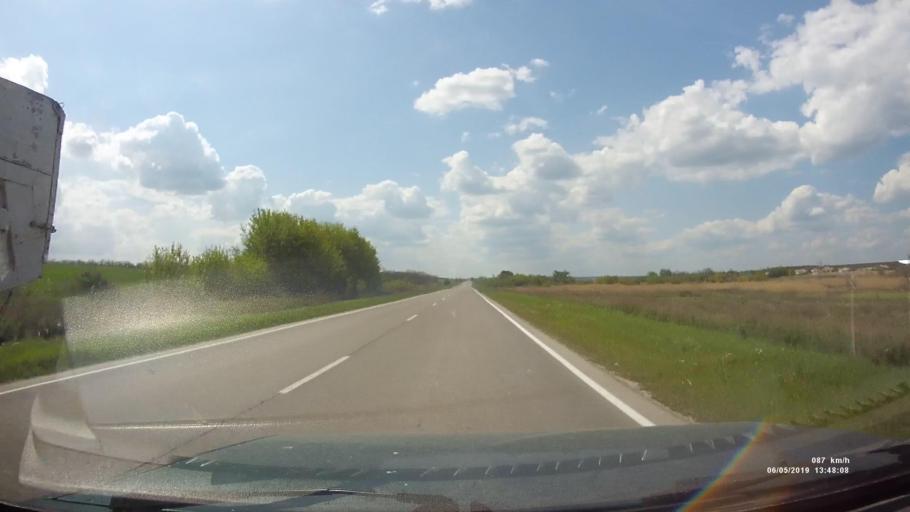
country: RU
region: Rostov
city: Melikhovskaya
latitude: 47.6580
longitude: 40.5493
